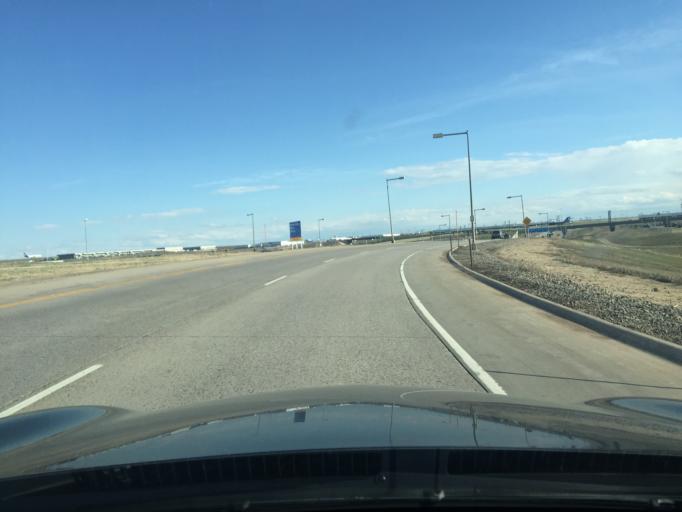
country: US
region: Colorado
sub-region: Weld County
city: Lochbuie
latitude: 39.8420
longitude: -104.6764
